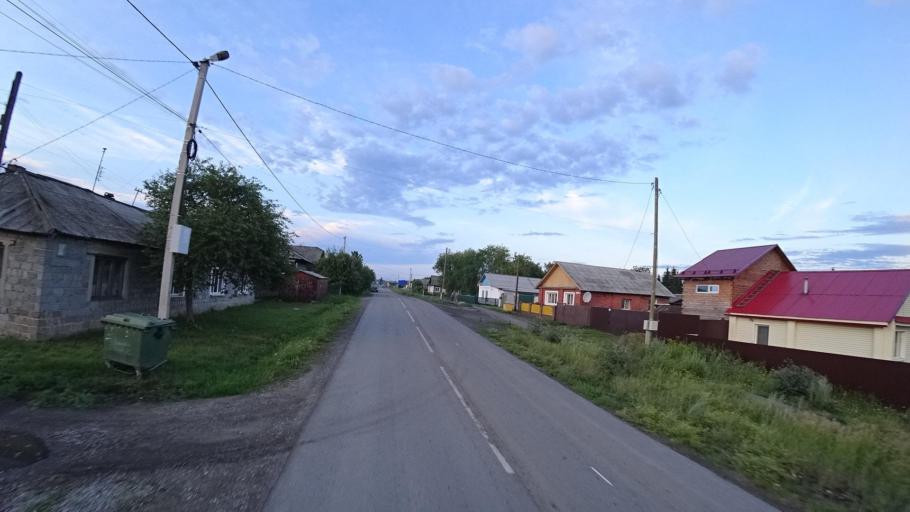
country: RU
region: Sverdlovsk
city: Kamyshlov
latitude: 56.8557
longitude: 62.6979
